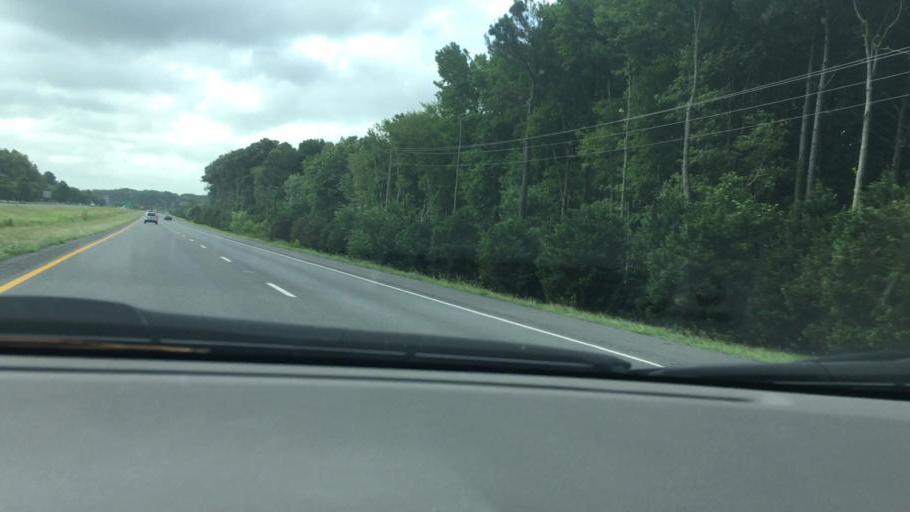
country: US
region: Maryland
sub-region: Worcester County
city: Pocomoke City
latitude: 38.0683
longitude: -75.5515
